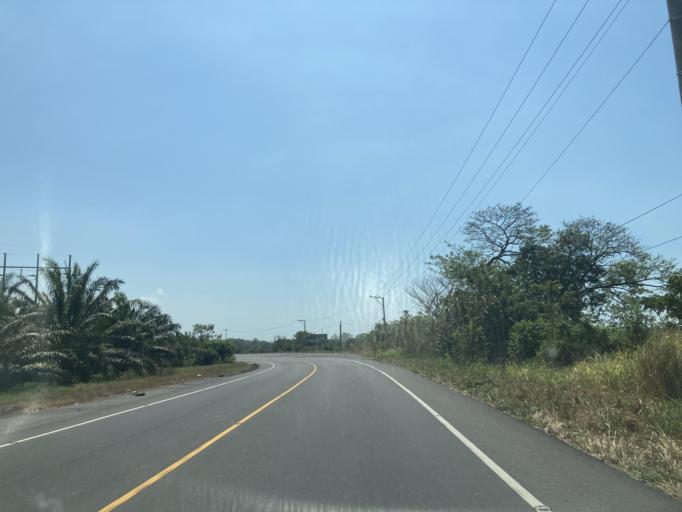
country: GT
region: Escuintla
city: Guanagazapa
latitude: 14.1085
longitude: -90.6314
